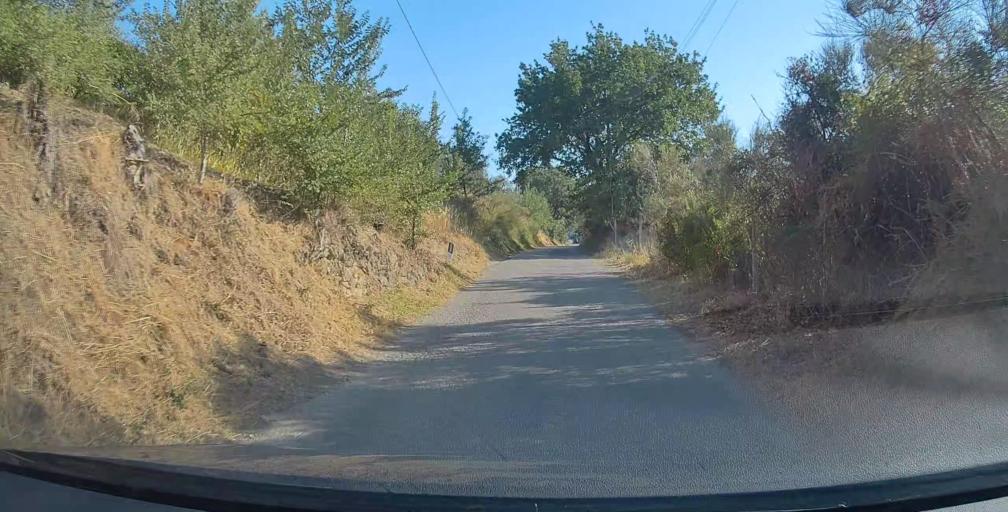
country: IT
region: Umbria
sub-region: Provincia di Terni
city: Calvi dell'Umbria
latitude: 42.3785
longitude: 12.5679
